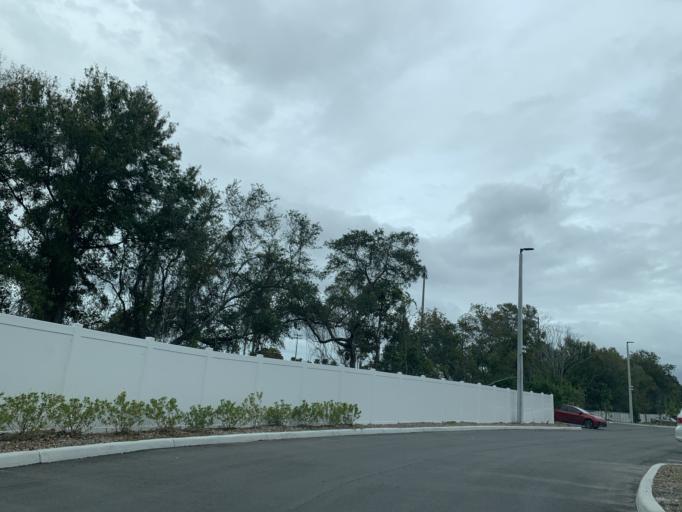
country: US
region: Florida
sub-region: Pinellas County
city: Belleair
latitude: 27.9442
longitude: -82.7957
